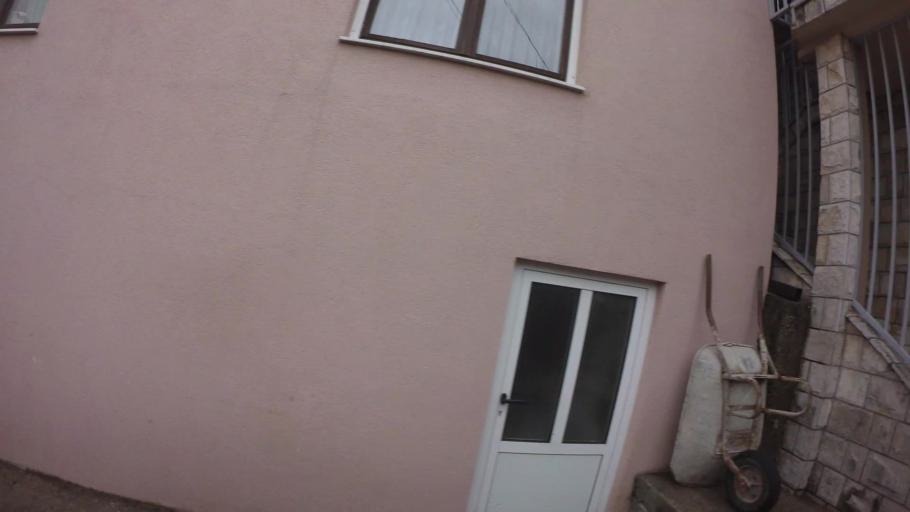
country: BA
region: Federation of Bosnia and Herzegovina
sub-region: Hercegovacko-Bosanski Kanton
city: Mostar
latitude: 43.3315
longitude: 17.7971
